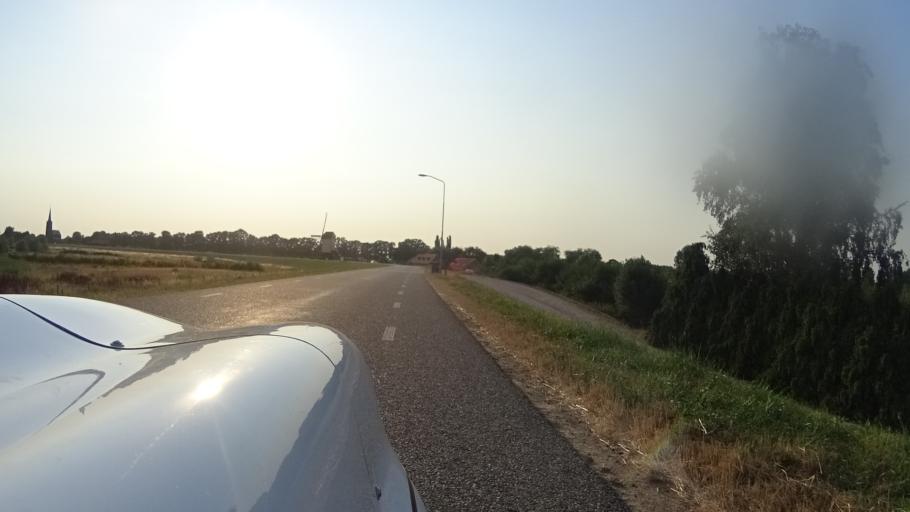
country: NL
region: Gelderland
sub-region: Gemeente Wijchen
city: Bergharen
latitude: 51.8238
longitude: 5.6428
